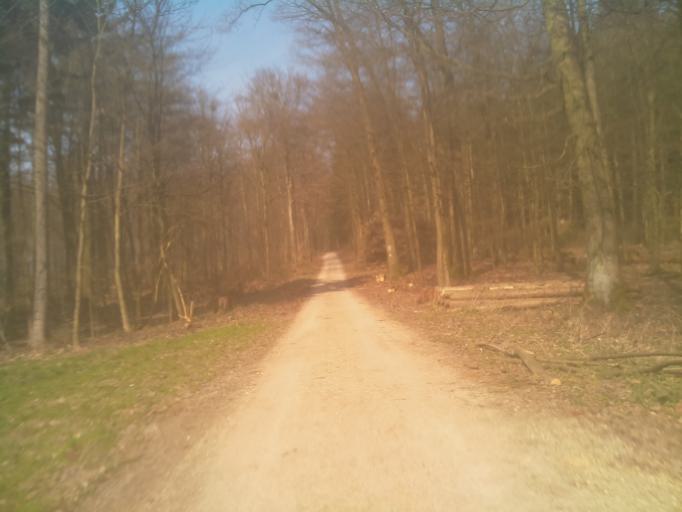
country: DE
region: Hesse
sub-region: Regierungsbezirk Darmstadt
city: Birkenau
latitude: 49.5781
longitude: 8.6839
